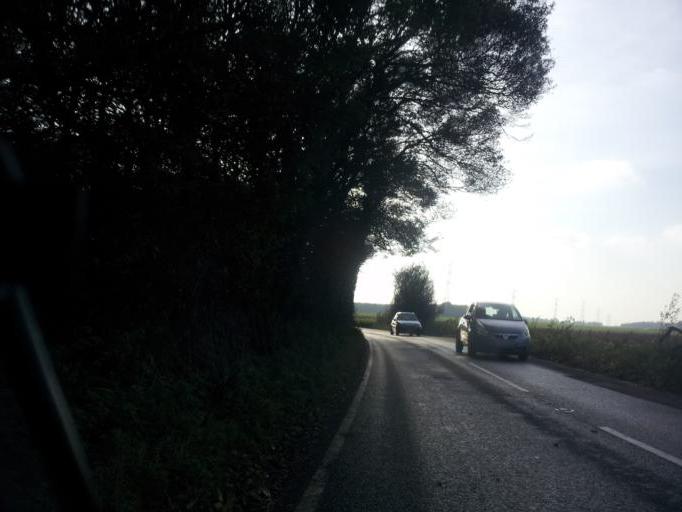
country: GB
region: England
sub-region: Kent
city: Boxley
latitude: 51.3215
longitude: 0.5576
